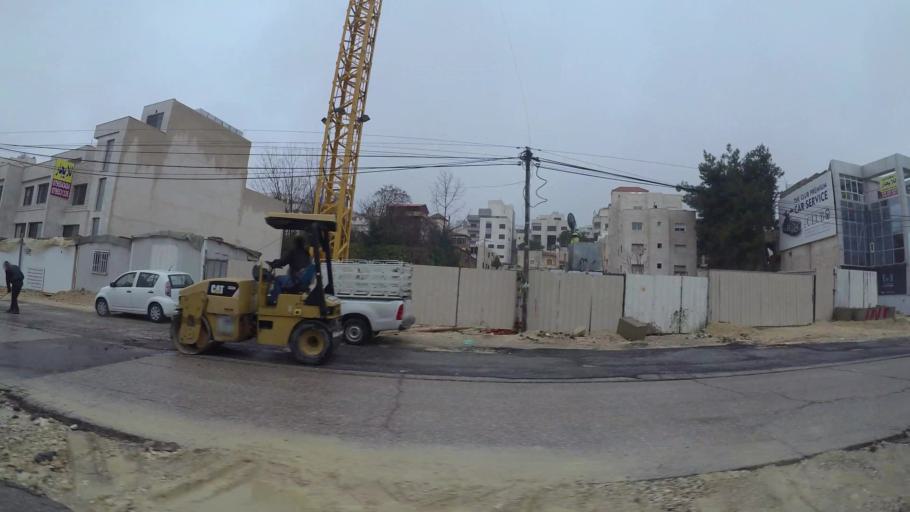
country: JO
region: Amman
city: Al Jubayhah
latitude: 32.0149
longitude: 35.8337
